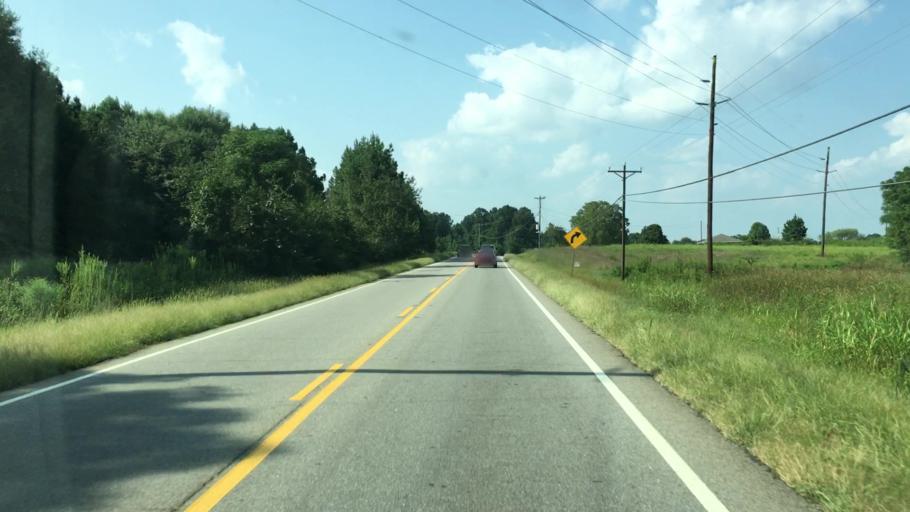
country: US
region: Georgia
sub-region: Walton County
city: Social Circle
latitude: 33.7025
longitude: -83.7023
